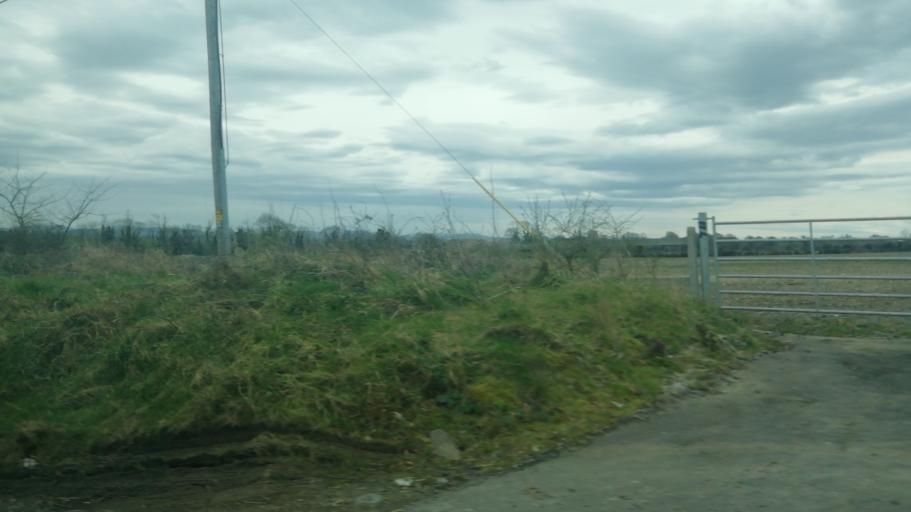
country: IE
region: Leinster
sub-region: Kildare
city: Celbridge
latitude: 53.3245
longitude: -6.5955
